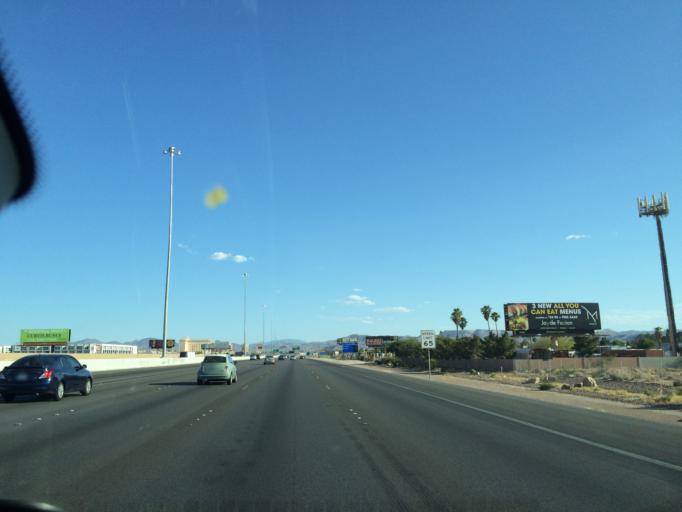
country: US
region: Nevada
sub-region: Clark County
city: Enterprise
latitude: 36.0338
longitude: -115.1810
